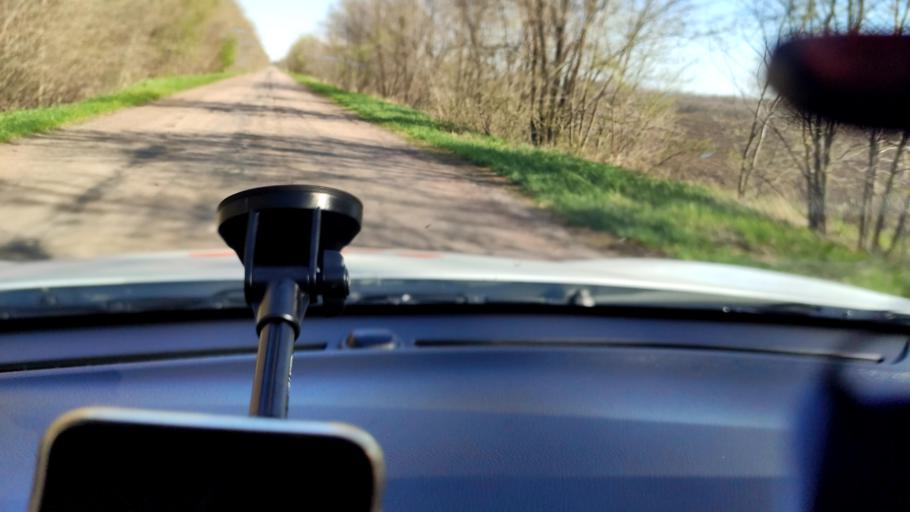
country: RU
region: Voronezj
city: Uryv-Pokrovka
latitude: 51.1319
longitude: 39.0976
